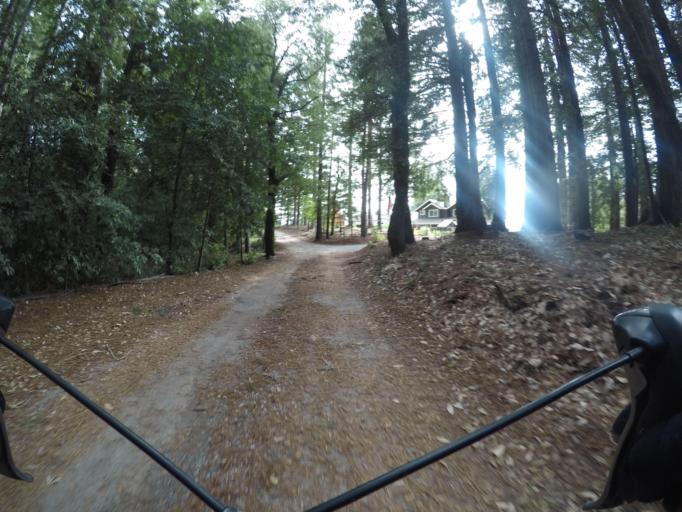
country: US
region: California
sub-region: Santa Cruz County
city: Brookdale
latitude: 37.1118
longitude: -122.0956
